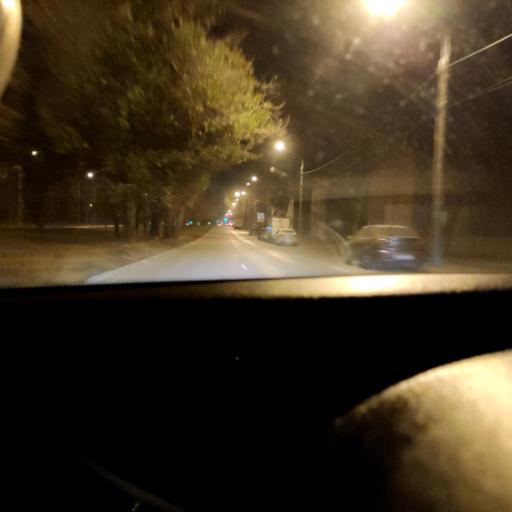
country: RU
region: Samara
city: Samara
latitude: 53.2207
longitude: 50.2383
